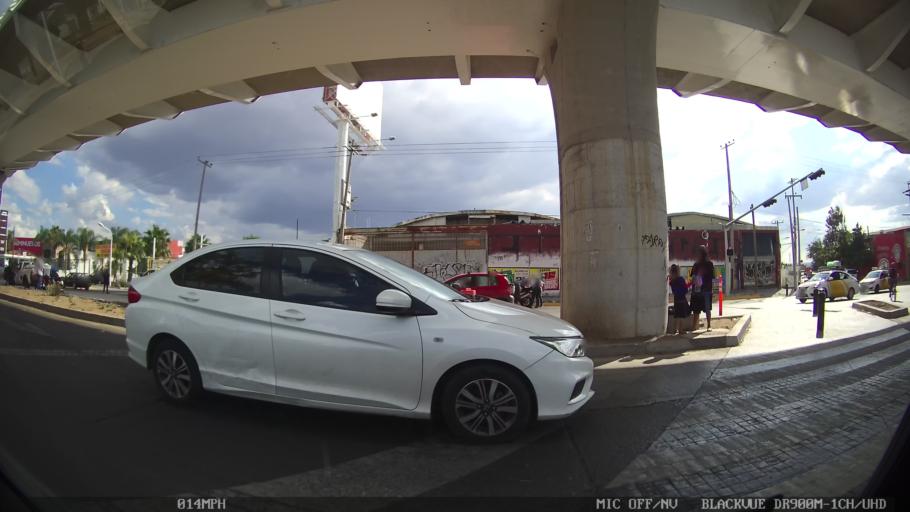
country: MX
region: Jalisco
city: Tlaquepaque
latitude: 20.6336
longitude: -103.2971
